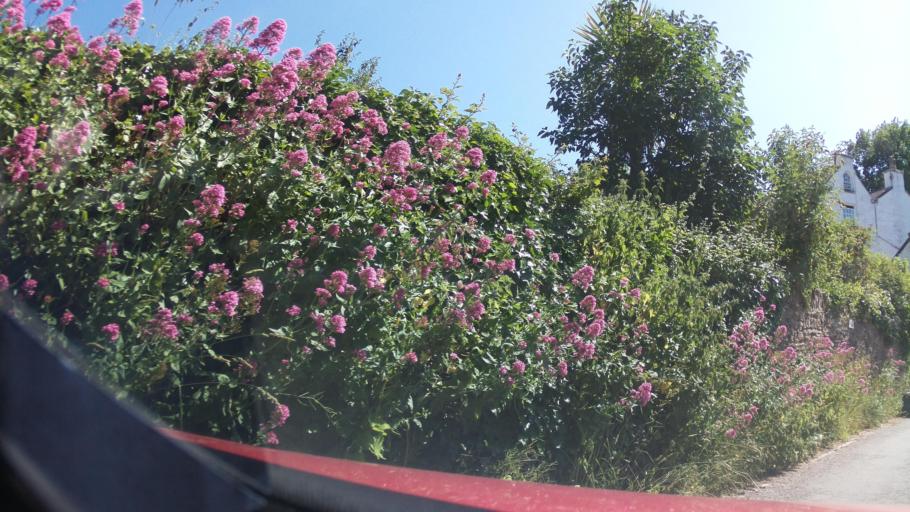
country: GB
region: England
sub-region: Devon
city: Marldon
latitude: 50.4695
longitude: -3.5944
